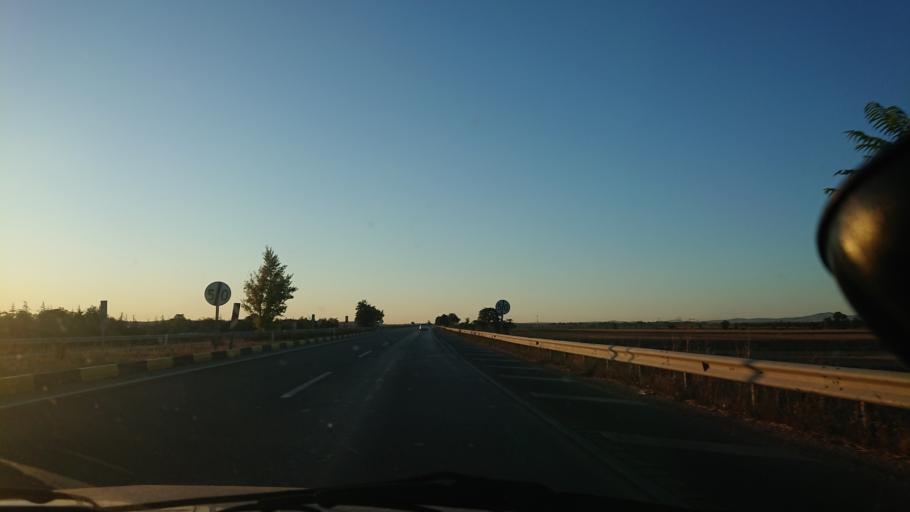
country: TR
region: Eskisehir
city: Mahmudiye
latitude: 39.5397
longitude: 30.9407
